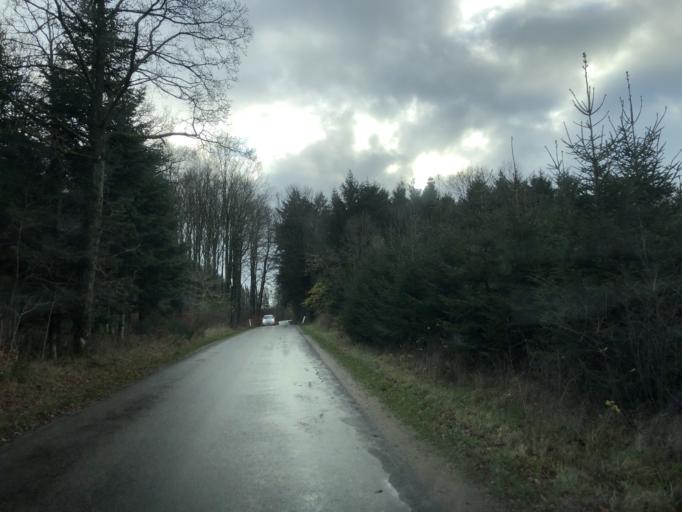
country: DK
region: North Denmark
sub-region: Rebild Kommune
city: Stovring
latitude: 56.9264
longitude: 9.8048
